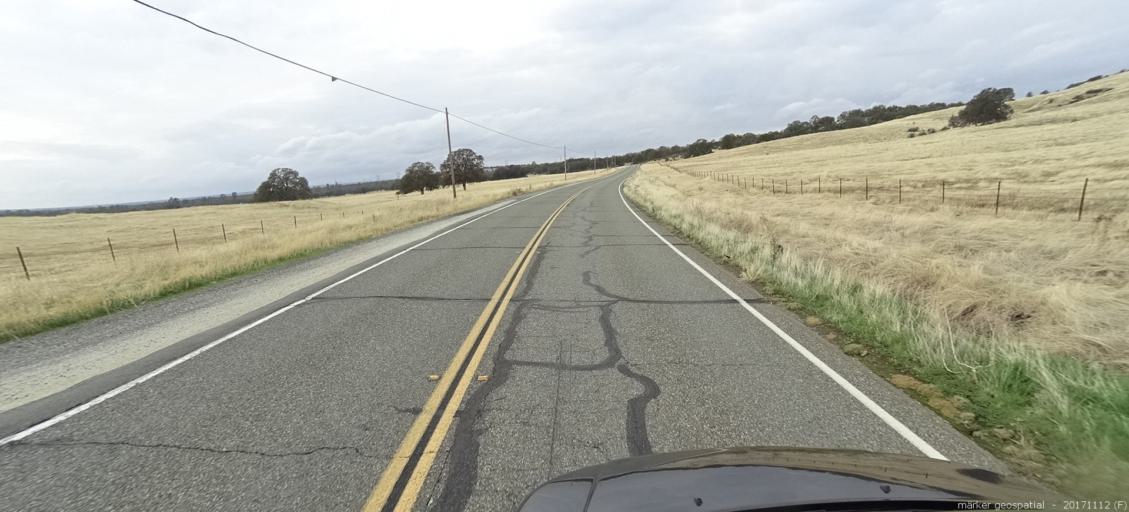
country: US
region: California
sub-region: Shasta County
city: Palo Cedro
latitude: 40.4764
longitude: -122.1813
